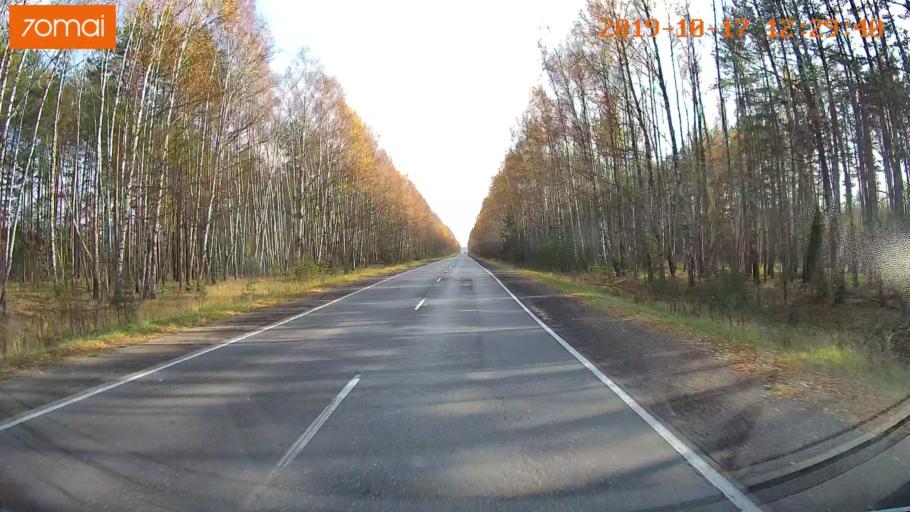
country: RU
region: Rjazan
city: Syntul
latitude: 54.9800
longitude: 41.2975
